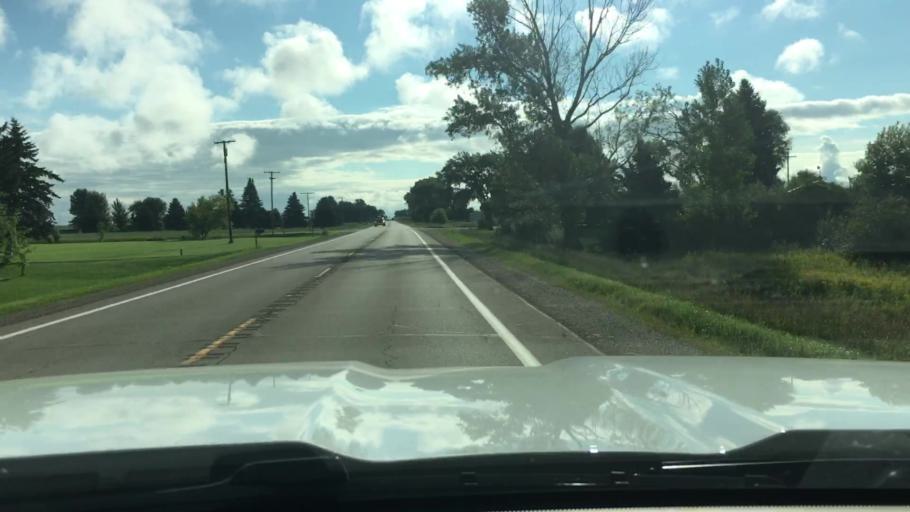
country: US
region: Michigan
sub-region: Tuscola County
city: Cass City
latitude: 43.5996
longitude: -83.2351
